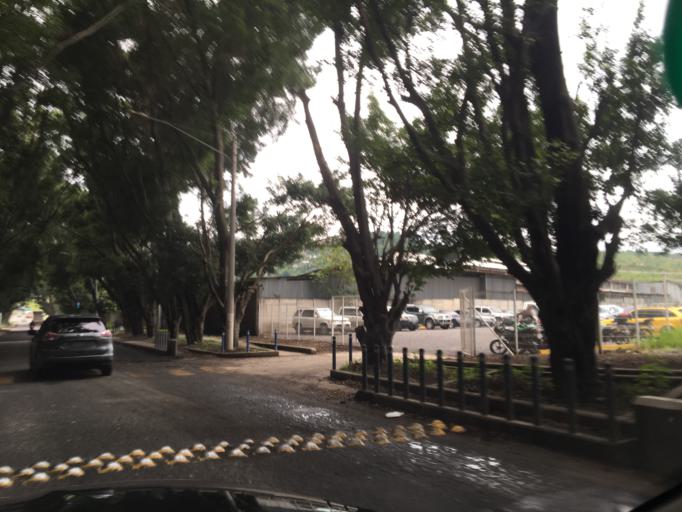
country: GT
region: Guatemala
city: Villa Nueva
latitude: 14.5096
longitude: -90.5849
